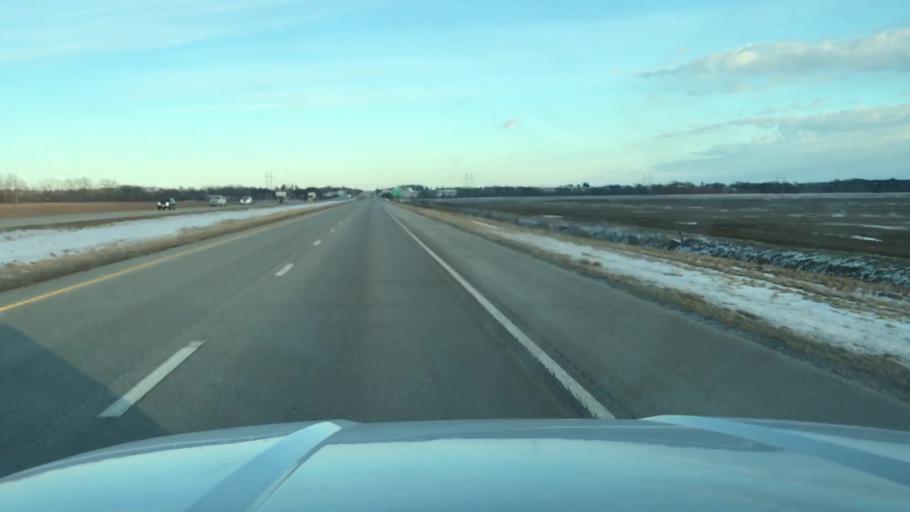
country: US
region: Missouri
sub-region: Buchanan County
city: Saint Joseph
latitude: 39.7478
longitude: -94.7404
